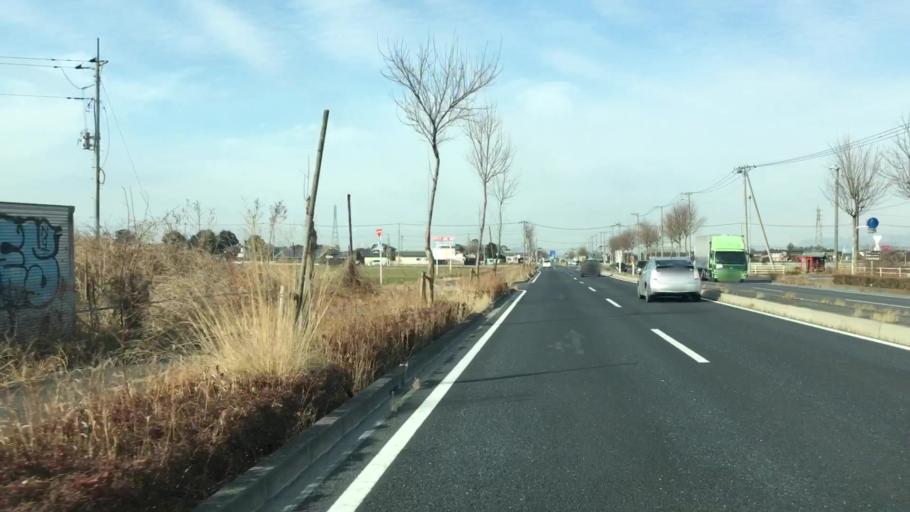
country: JP
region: Gunma
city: Tatebayashi
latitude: 36.2313
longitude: 139.4875
